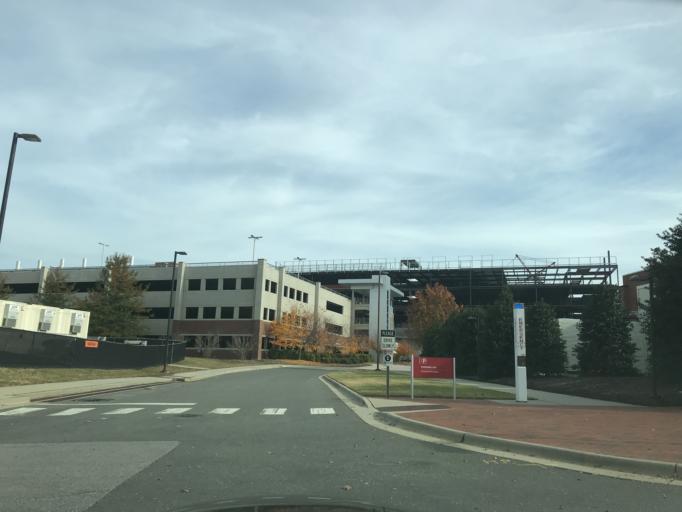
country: US
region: North Carolina
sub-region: Wake County
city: West Raleigh
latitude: 35.7713
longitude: -78.6777
